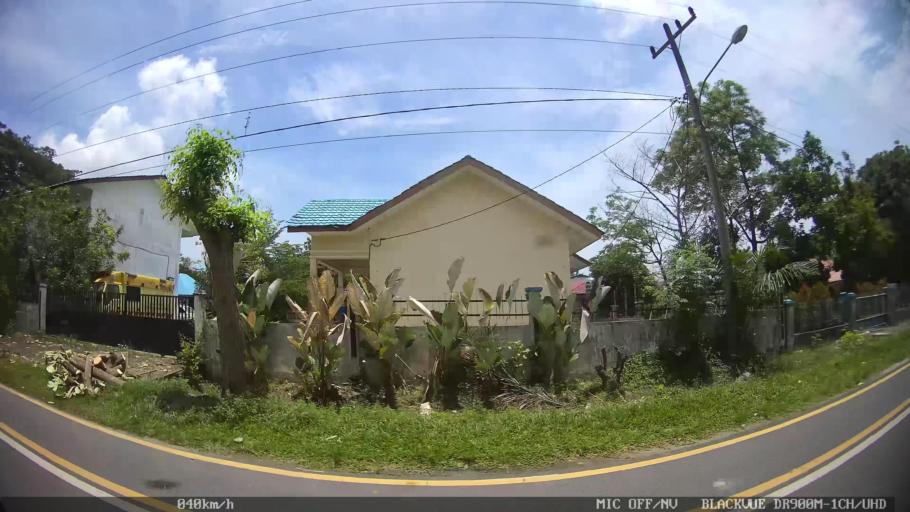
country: ID
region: North Sumatra
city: Percut
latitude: 3.5446
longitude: 98.8685
